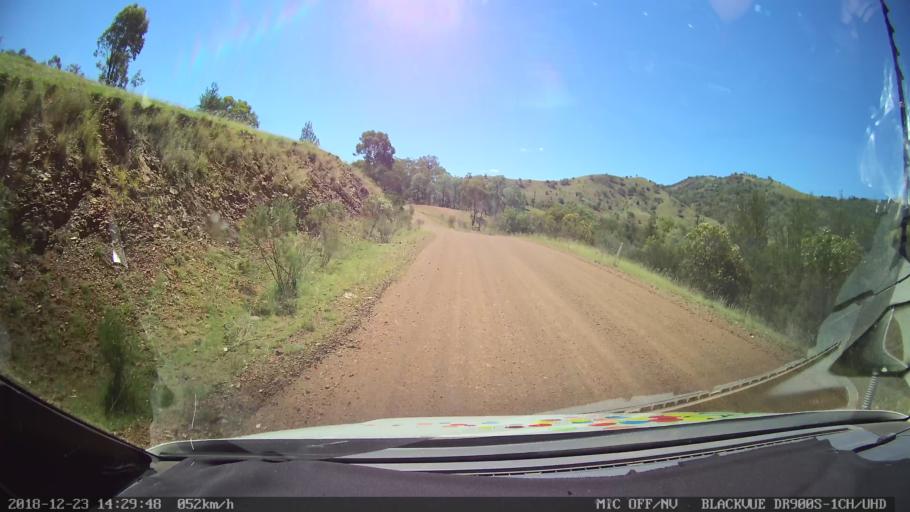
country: AU
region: New South Wales
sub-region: Tamworth Municipality
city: Manilla
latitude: -30.6061
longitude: 150.9362
